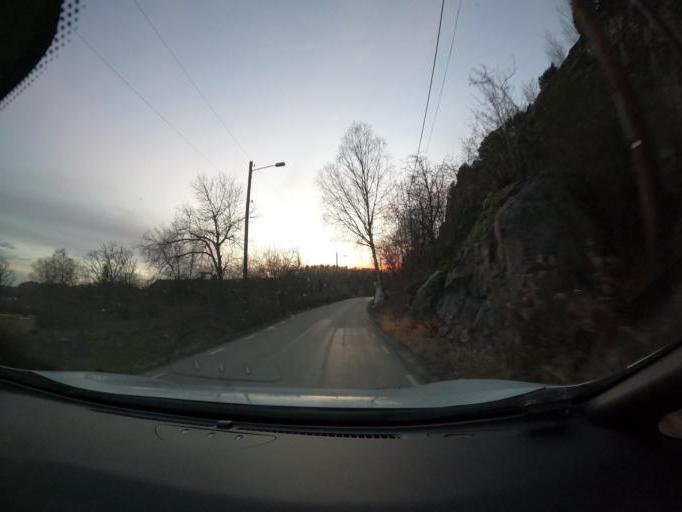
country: SE
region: Vaestra Goetaland
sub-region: Harryda Kommun
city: Molnlycke
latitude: 57.6059
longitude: 12.1423
